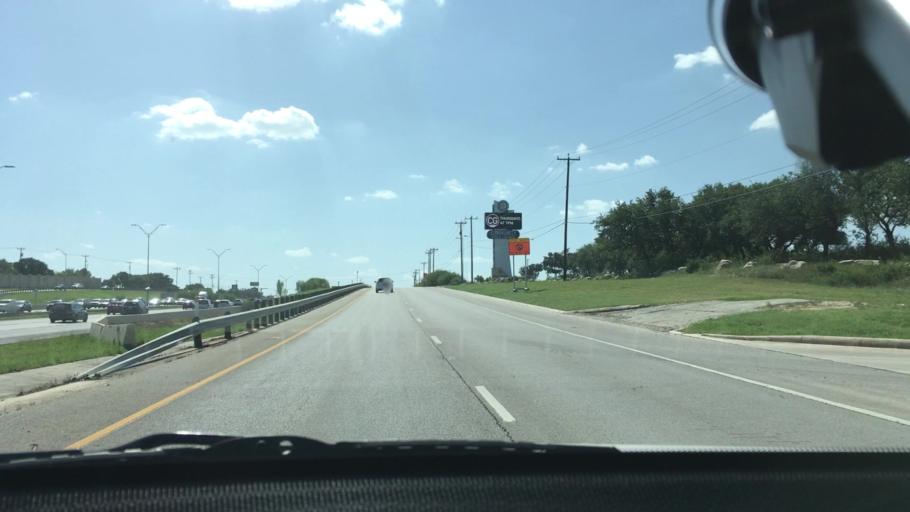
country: US
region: Texas
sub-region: Bexar County
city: Hollywood Park
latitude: 29.6056
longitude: -98.4526
